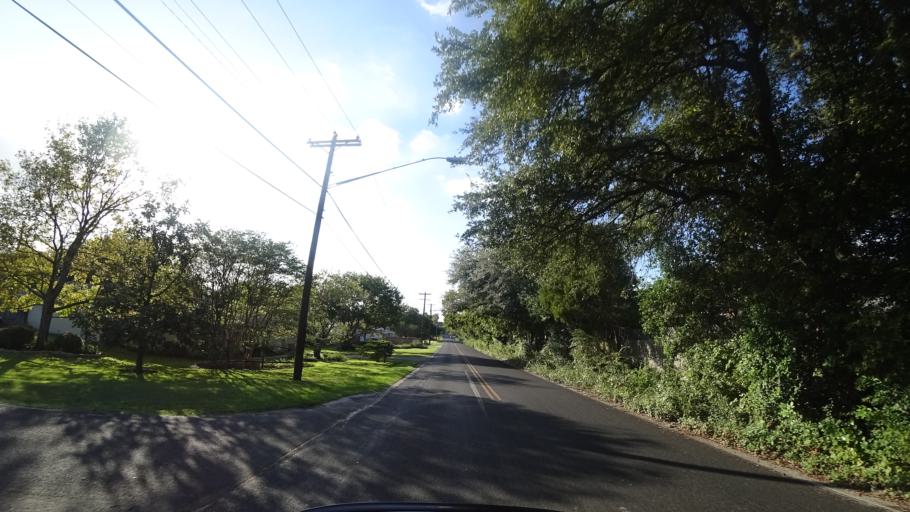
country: US
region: Texas
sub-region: Travis County
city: Onion Creek
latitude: 30.1942
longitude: -97.7953
